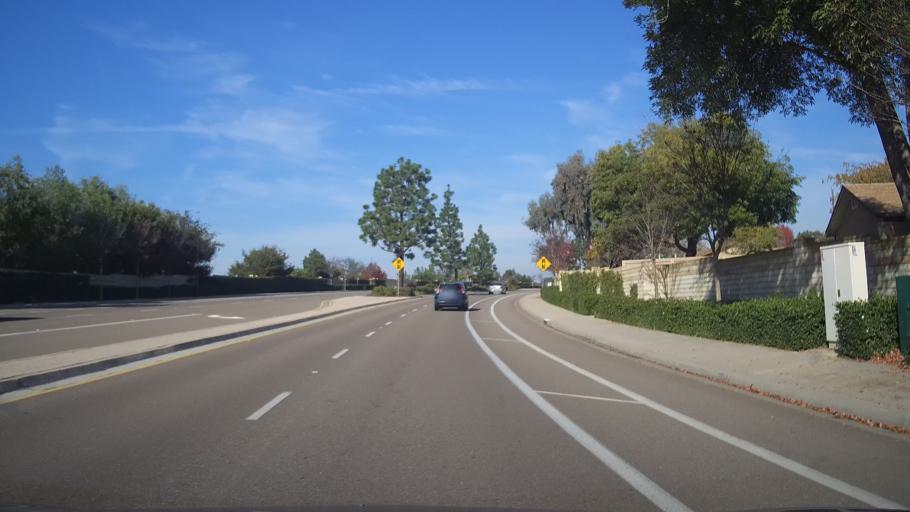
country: US
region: California
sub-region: San Diego County
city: La Mesa
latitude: 32.8130
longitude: -117.1059
